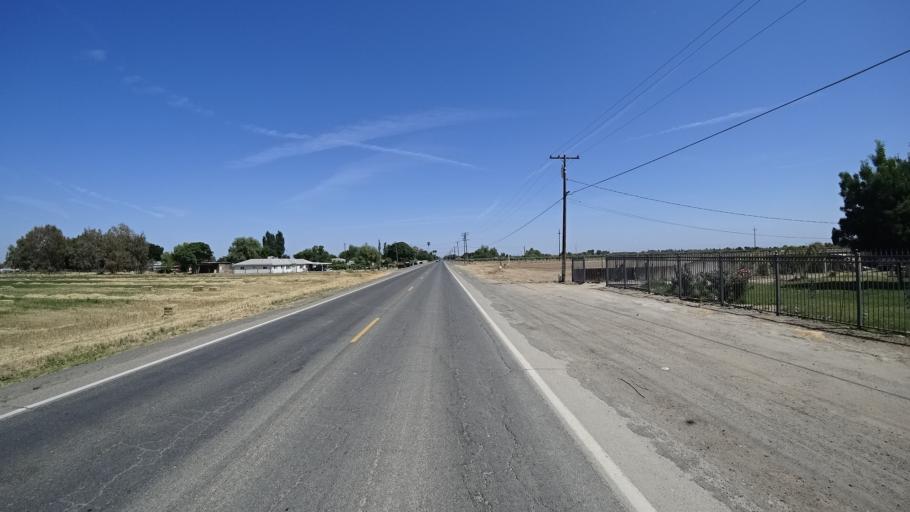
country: US
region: California
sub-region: Kings County
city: Lemoore
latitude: 36.2498
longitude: -119.7807
